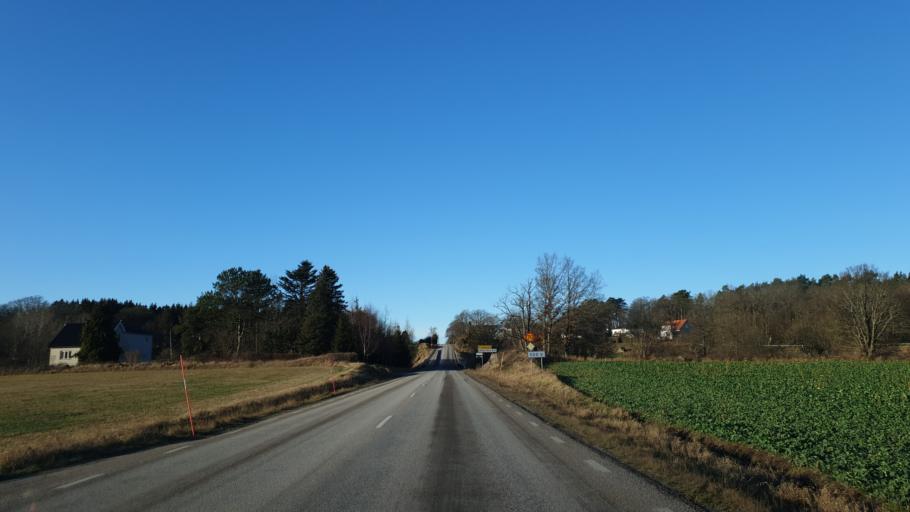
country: SE
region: Blekinge
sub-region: Ronneby Kommun
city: Ronneby
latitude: 56.1956
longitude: 15.3381
